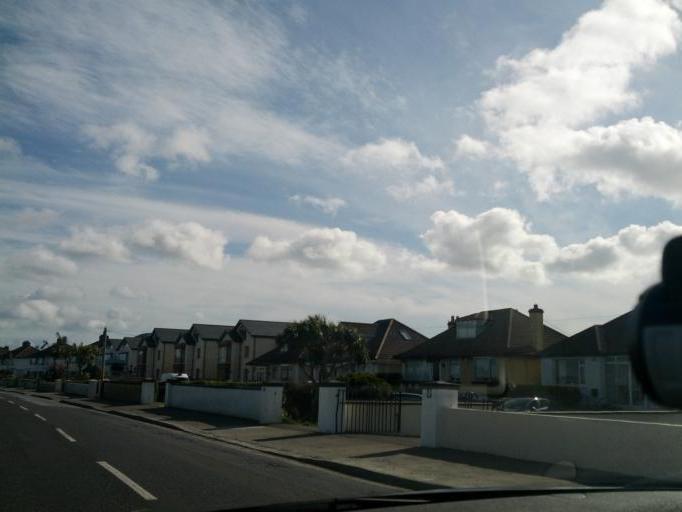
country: IE
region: Leinster
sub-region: Fingal County
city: Baldoyle
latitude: 53.3952
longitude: -6.1237
